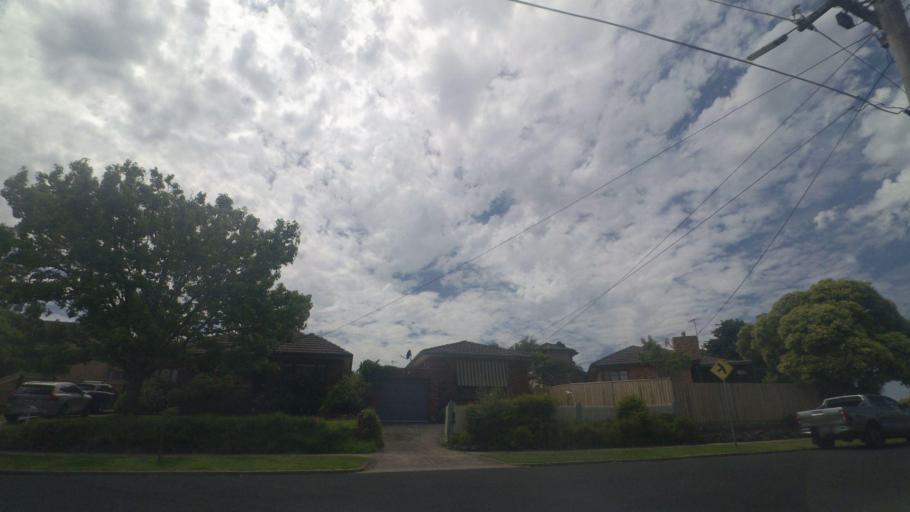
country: AU
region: Victoria
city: Rosanna
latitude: -37.7444
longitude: 145.0751
